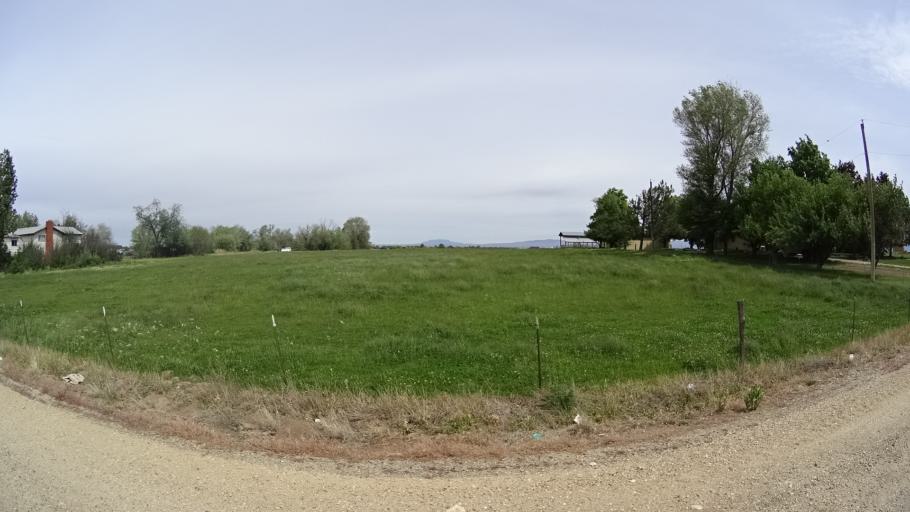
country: US
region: Idaho
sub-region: Ada County
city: Meridian
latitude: 43.5611
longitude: -116.4032
